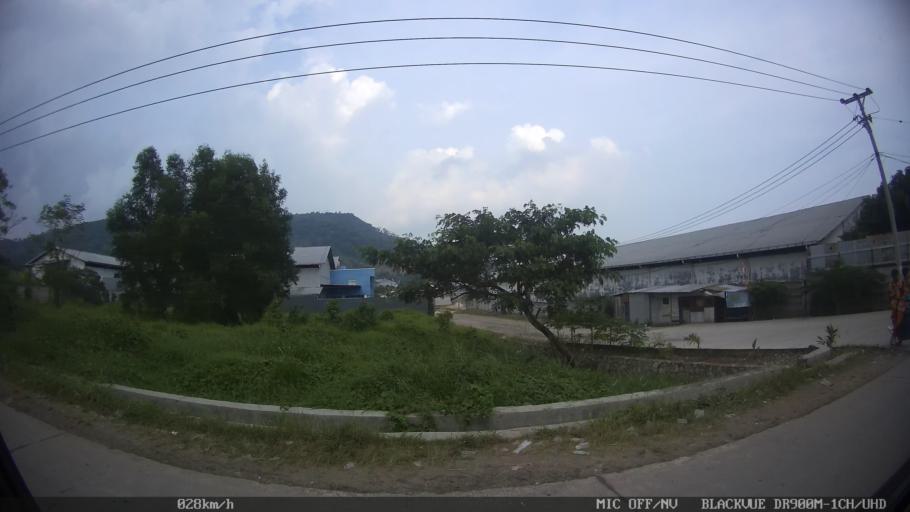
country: ID
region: Lampung
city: Bandarlampung
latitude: -5.4365
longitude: 105.2965
